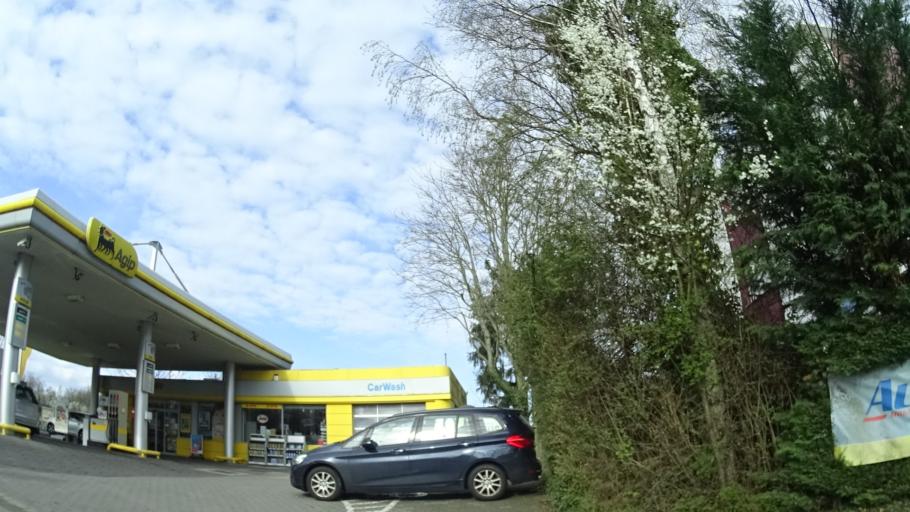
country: DE
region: Hesse
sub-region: Regierungsbezirk Darmstadt
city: Bad Vilbel
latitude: 50.1572
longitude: 8.7446
